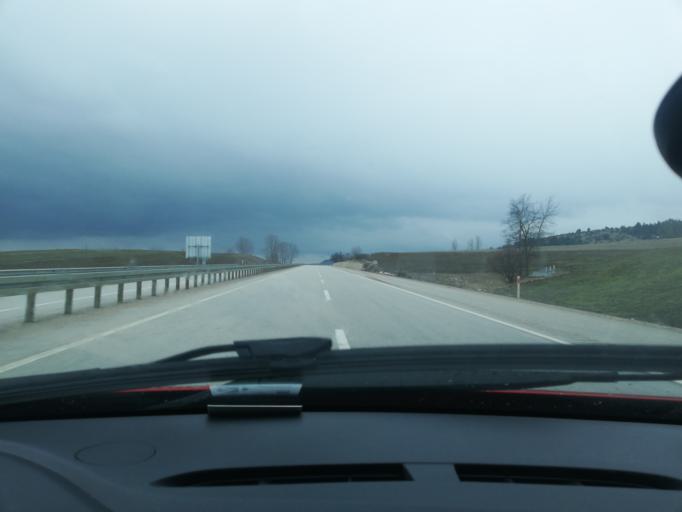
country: TR
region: Kastamonu
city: Seydiler
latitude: 41.6124
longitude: 33.7305
